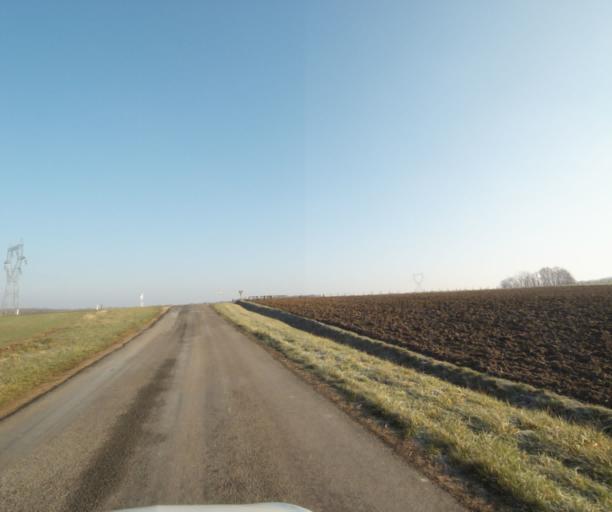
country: FR
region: Champagne-Ardenne
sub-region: Departement de la Haute-Marne
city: Montier-en-Der
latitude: 48.5061
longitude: 4.7311
